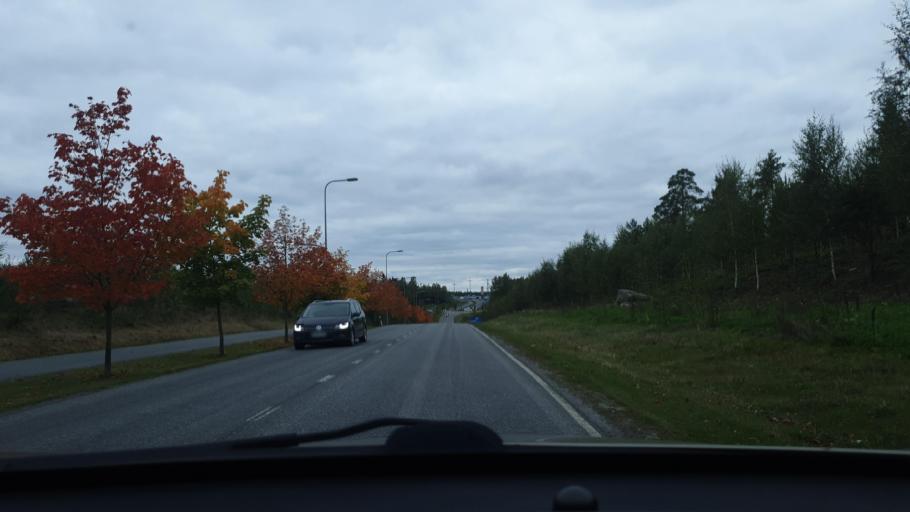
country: FI
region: Ostrobothnia
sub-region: Vaasa
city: Korsholm
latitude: 63.1070
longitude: 21.6713
